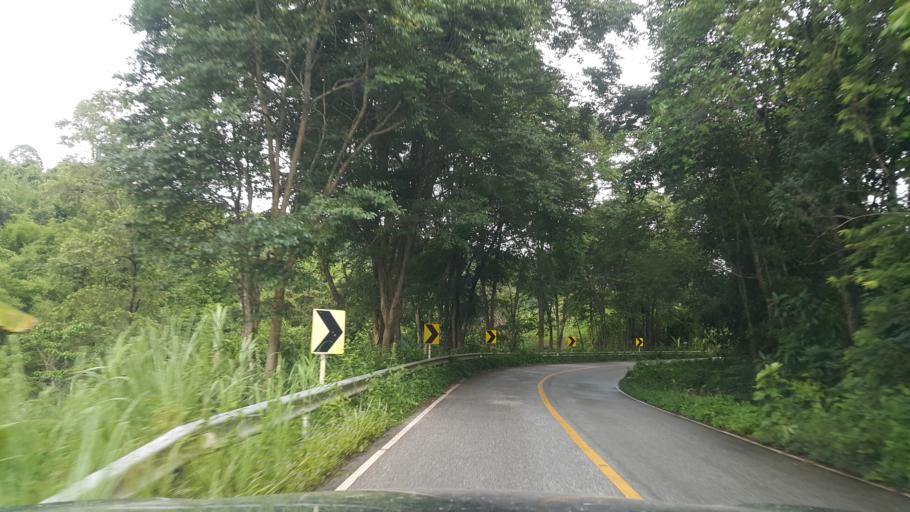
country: TH
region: Loei
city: Na Haeo
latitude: 17.4860
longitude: 100.8053
